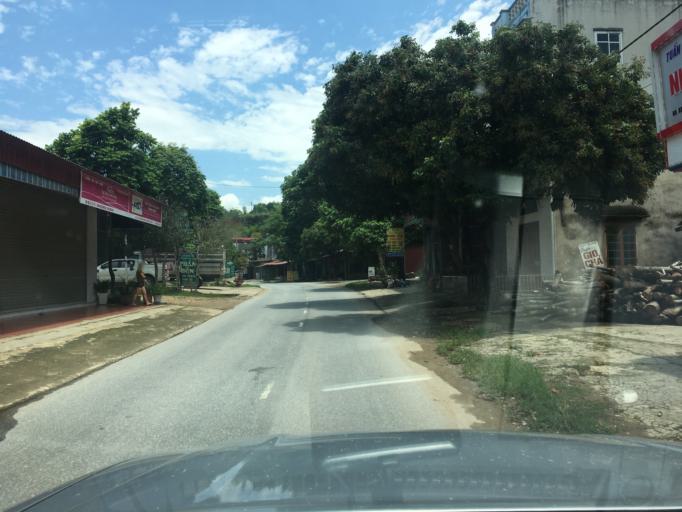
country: VN
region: Yen Bai
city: Son Thinh
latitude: 21.6502
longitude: 104.5008
